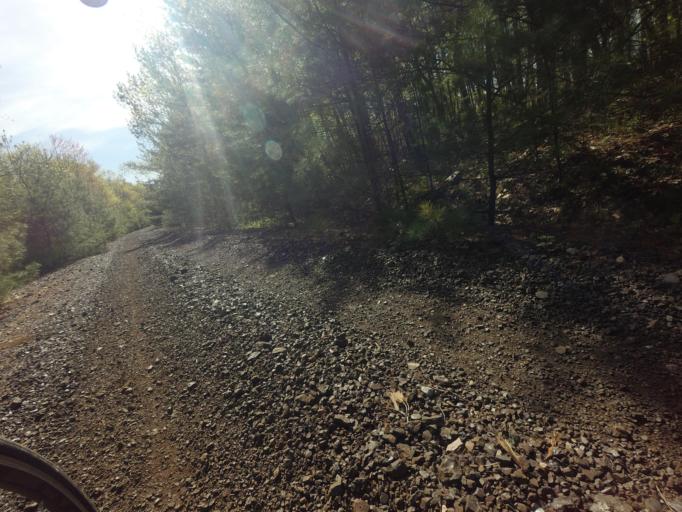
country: CA
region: Ontario
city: Arnprior
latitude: 45.4711
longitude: -76.2924
